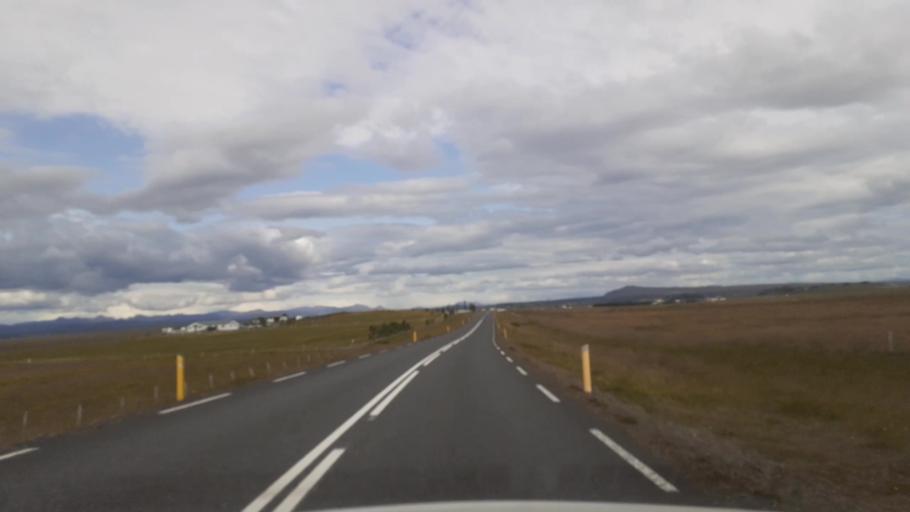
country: IS
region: South
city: Selfoss
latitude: 63.9263
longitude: -20.8508
